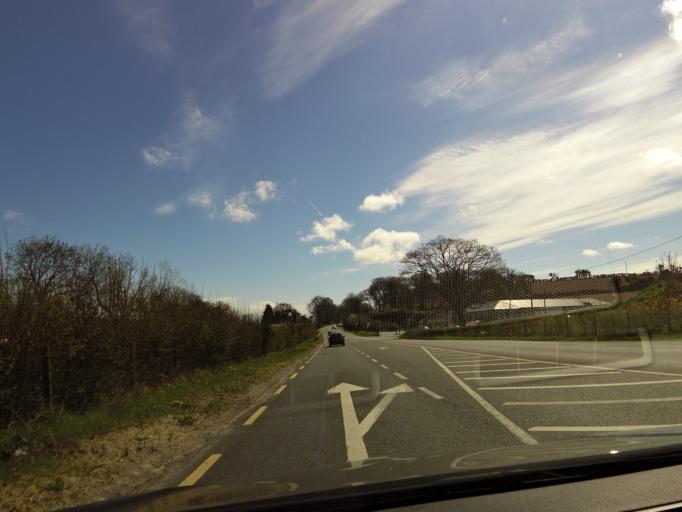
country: IE
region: Leinster
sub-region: Wicklow
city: Rathnew
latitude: 52.9254
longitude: -6.1164
